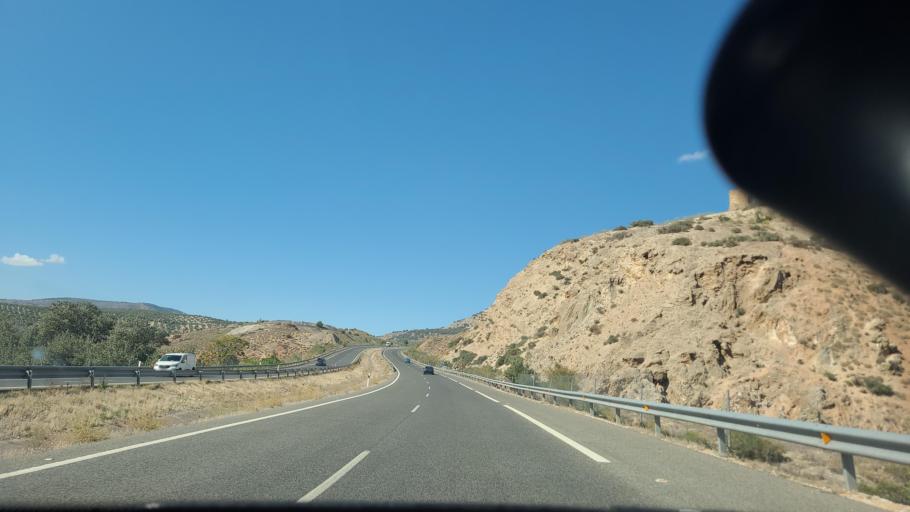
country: ES
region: Andalusia
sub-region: Provincia de Jaen
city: Pegalajar
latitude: 37.7107
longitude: -3.6408
